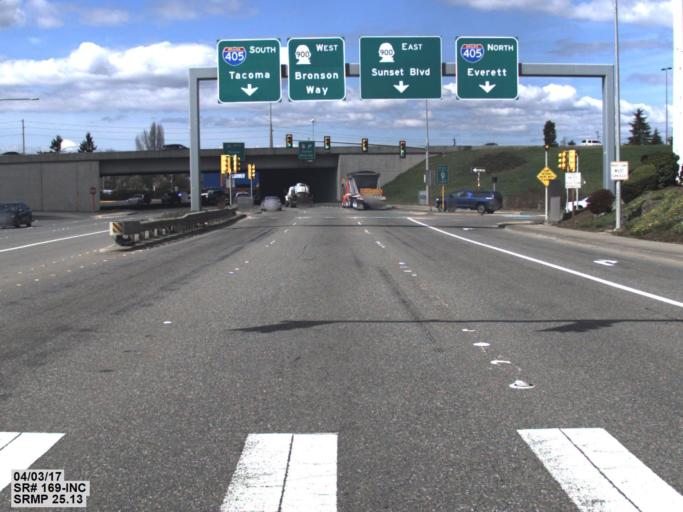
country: US
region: Washington
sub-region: King County
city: Renton
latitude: 47.4829
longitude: -122.1949
